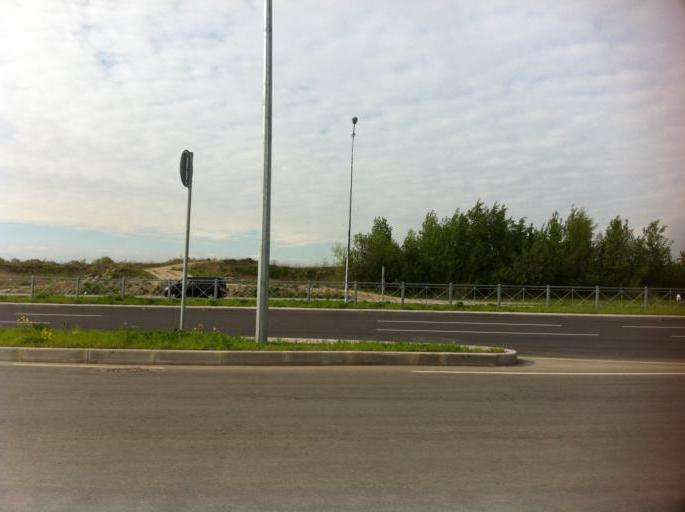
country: RU
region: St.-Petersburg
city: Sosnovaya Polyana
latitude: 59.8573
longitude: 30.1453
